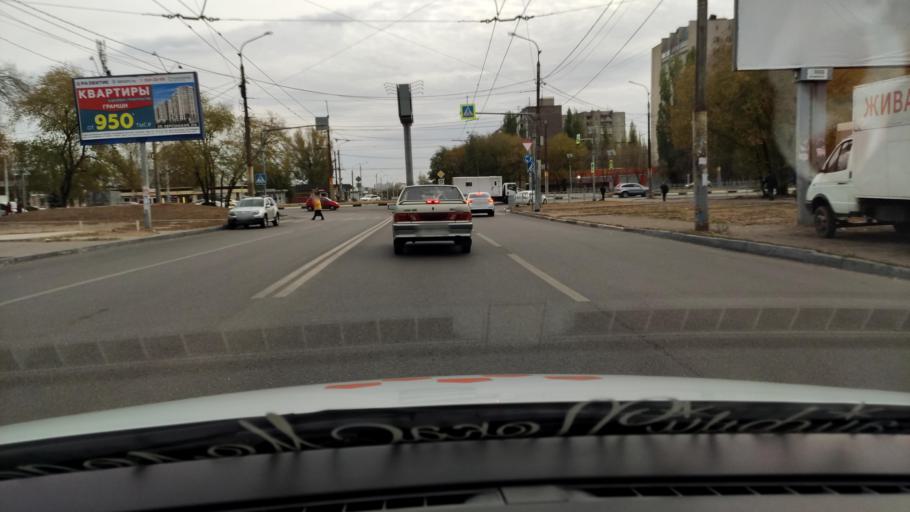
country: RU
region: Voronezj
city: Podgornoye
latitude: 51.7020
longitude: 39.1484
